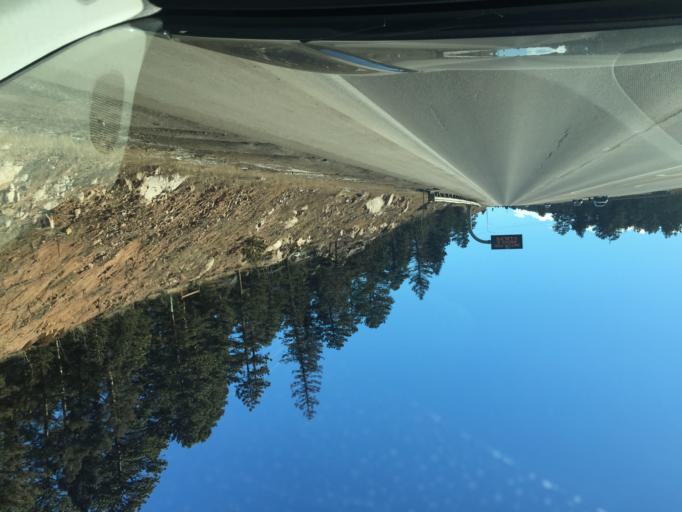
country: US
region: Colorado
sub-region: Jefferson County
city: Evergreen
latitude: 39.5042
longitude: -105.3178
